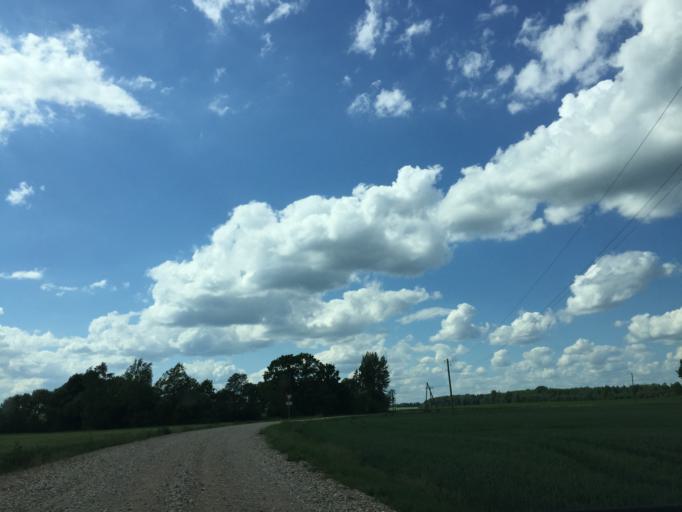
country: LV
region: Engure
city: Smarde
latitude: 56.8696
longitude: 23.3492
